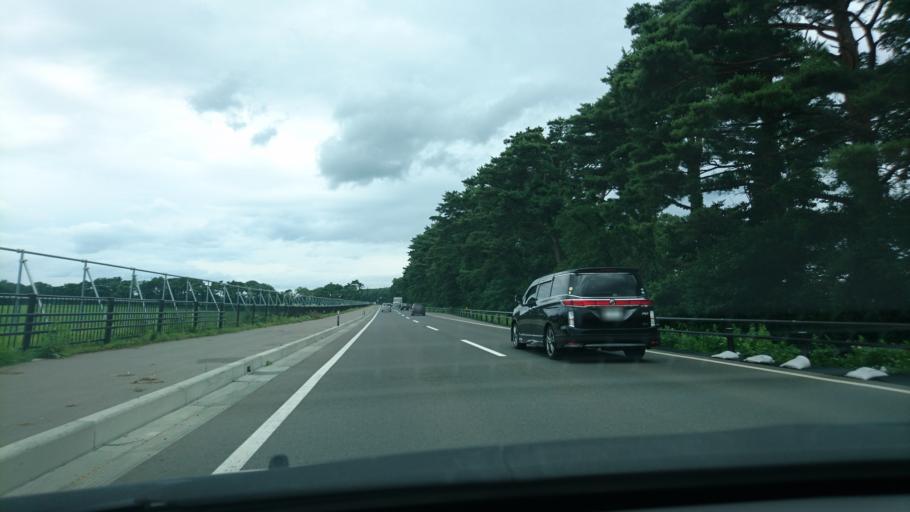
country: JP
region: Iwate
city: Morioka-shi
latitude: 39.7790
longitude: 141.1259
